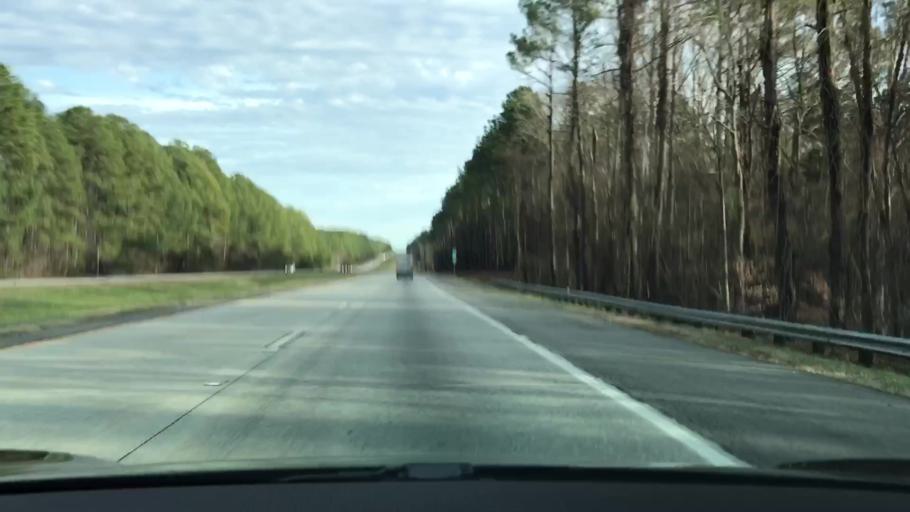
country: US
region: Georgia
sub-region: Taliaferro County
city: Crawfordville
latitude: 33.5226
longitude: -82.8728
